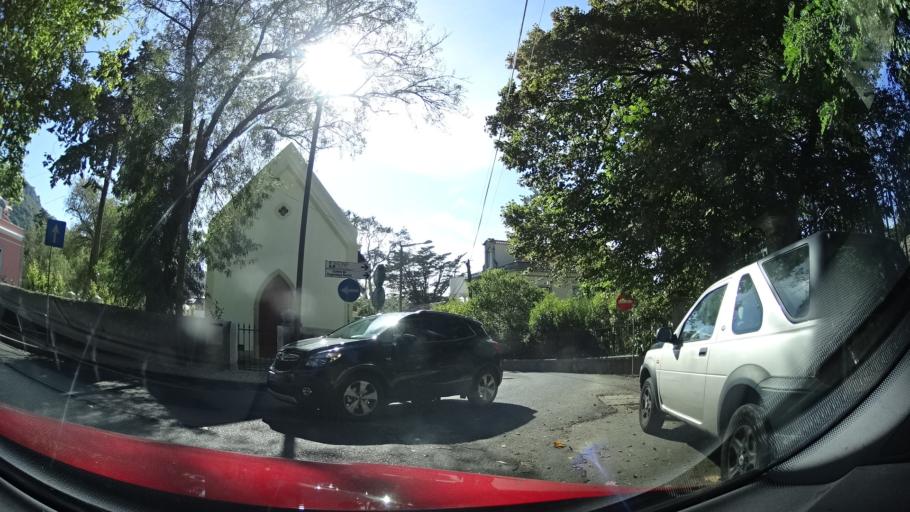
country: PT
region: Lisbon
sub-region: Sintra
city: Sintra
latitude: 38.8026
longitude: -9.3865
